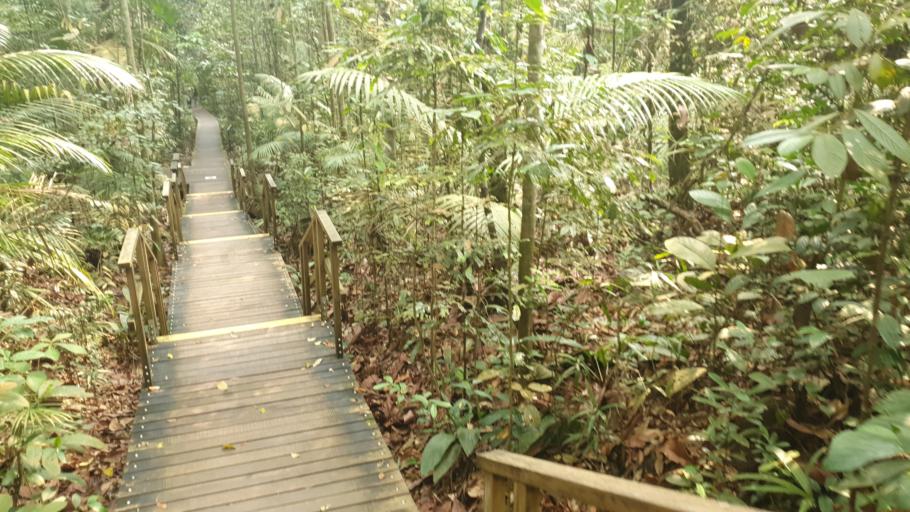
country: SG
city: Singapore
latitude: 1.3600
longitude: 103.8087
